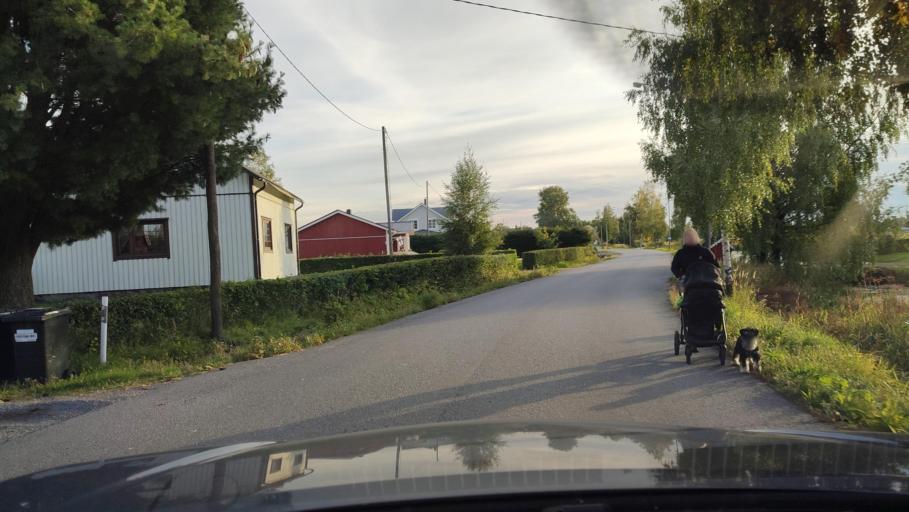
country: FI
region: Ostrobothnia
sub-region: Sydosterbotten
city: Kristinestad
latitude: 62.2477
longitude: 21.5063
